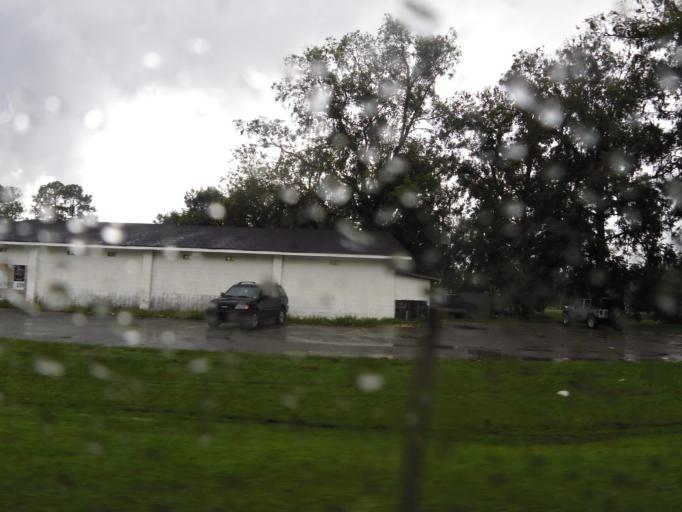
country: US
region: Florida
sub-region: Nassau County
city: Hilliard
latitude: 30.5225
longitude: -82.0372
